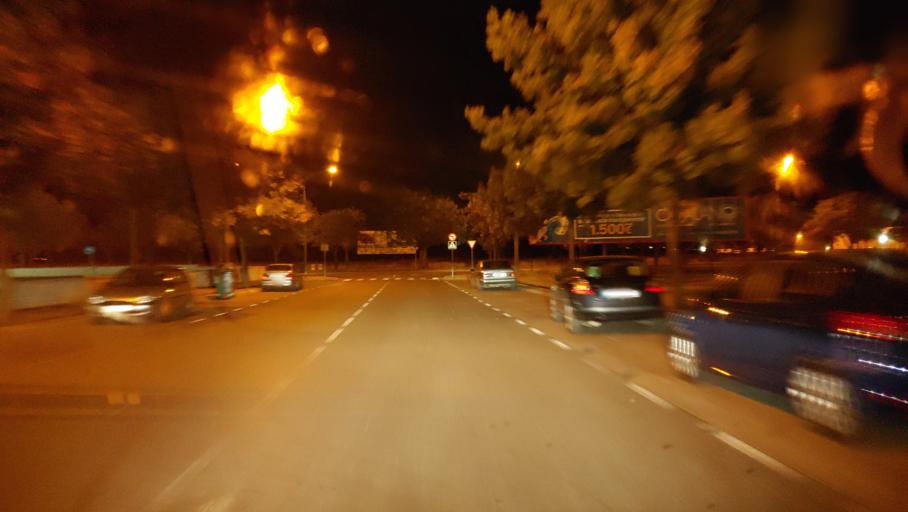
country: ES
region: Castille-La Mancha
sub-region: Provincia de Ciudad Real
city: Ciudad Real
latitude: 38.9852
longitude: -3.9072
